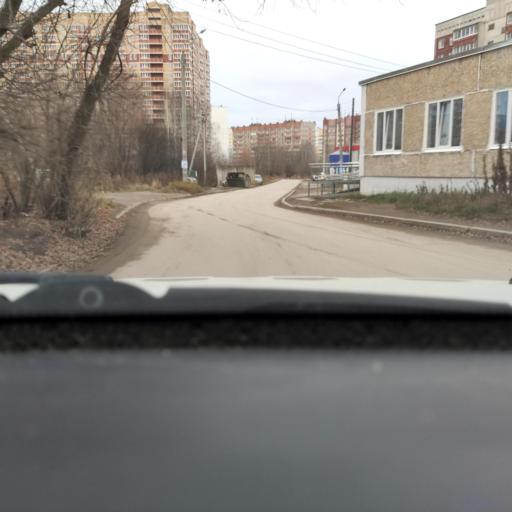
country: RU
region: Perm
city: Kondratovo
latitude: 58.0303
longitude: 56.0248
